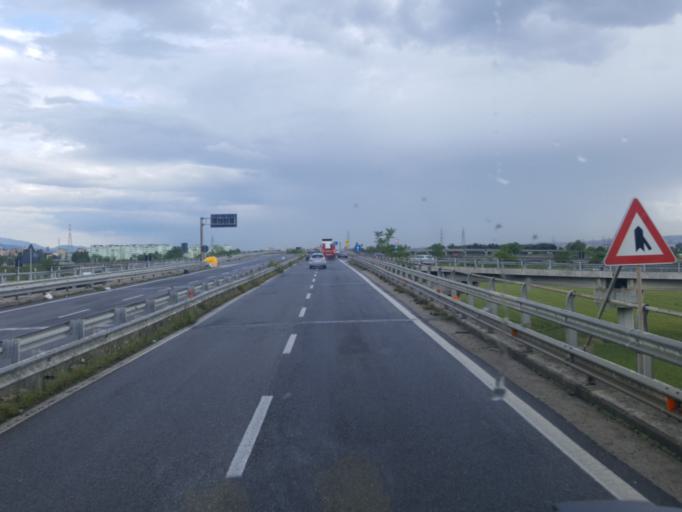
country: IT
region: Campania
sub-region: Provincia di Napoli
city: Pascarola
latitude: 40.9755
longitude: 14.2931
